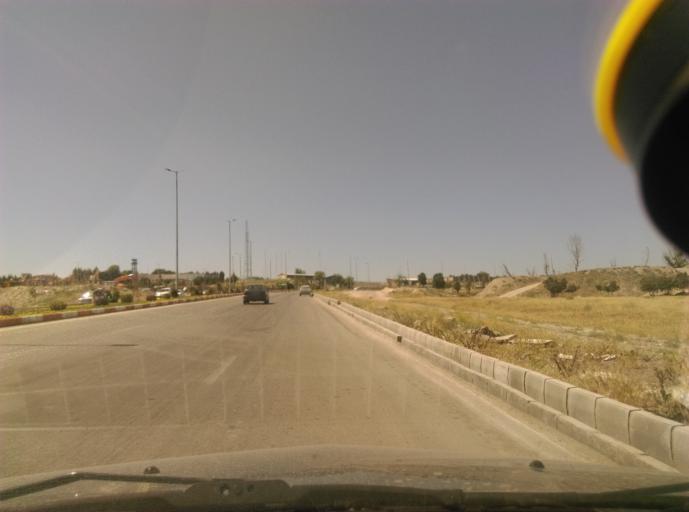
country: IR
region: Ardabil
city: Ardabil
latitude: 38.2237
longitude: 48.2792
